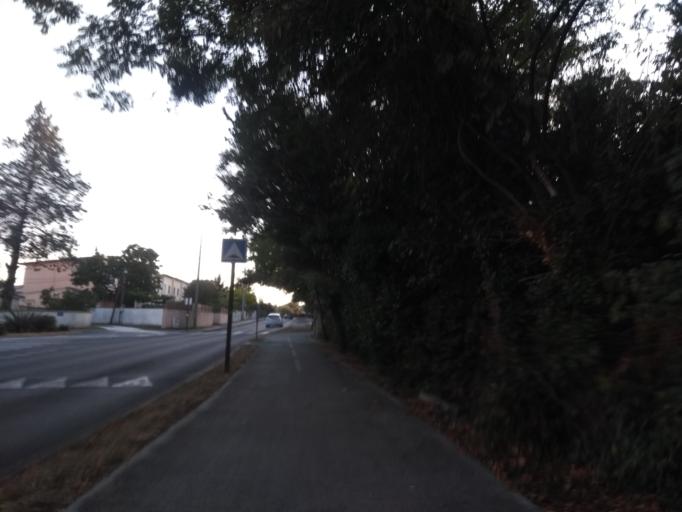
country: FR
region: Aquitaine
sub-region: Departement de la Gironde
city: Gradignan
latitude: 44.7826
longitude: -0.6140
